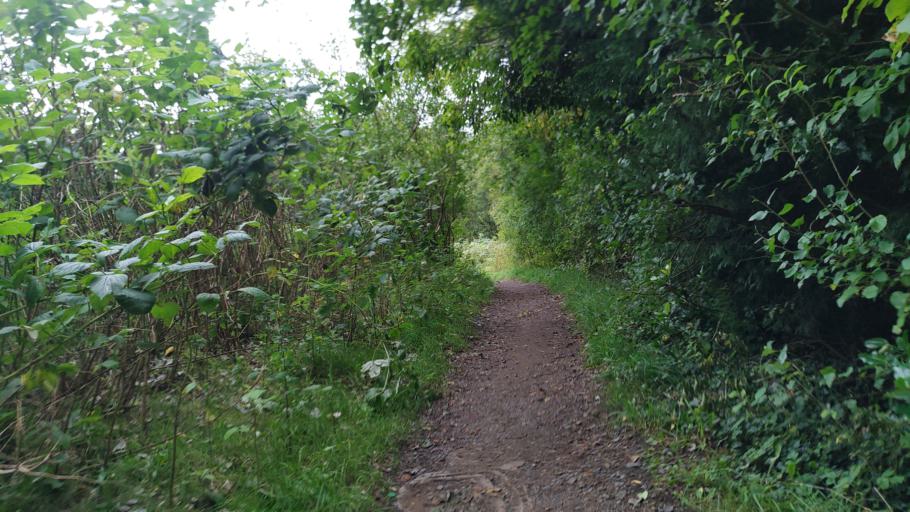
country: GB
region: England
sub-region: Lancashire
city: Clayton-le-Woods
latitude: 53.7119
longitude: -2.6481
